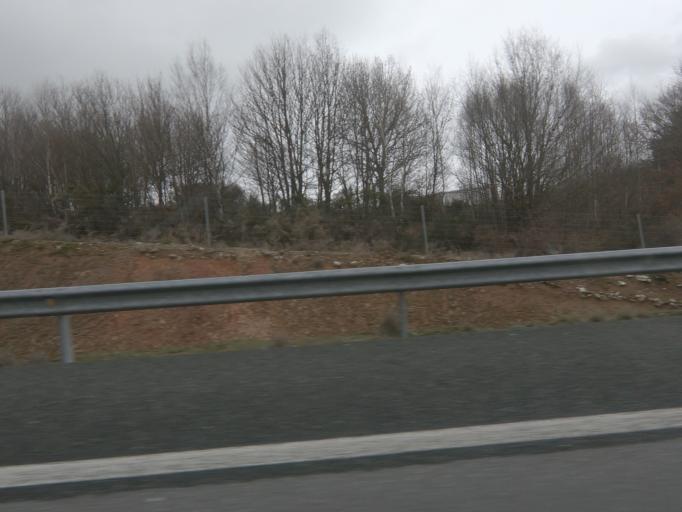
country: ES
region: Galicia
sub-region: Provincia de Pontevedra
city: Lalin
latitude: 42.6703
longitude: -8.1514
